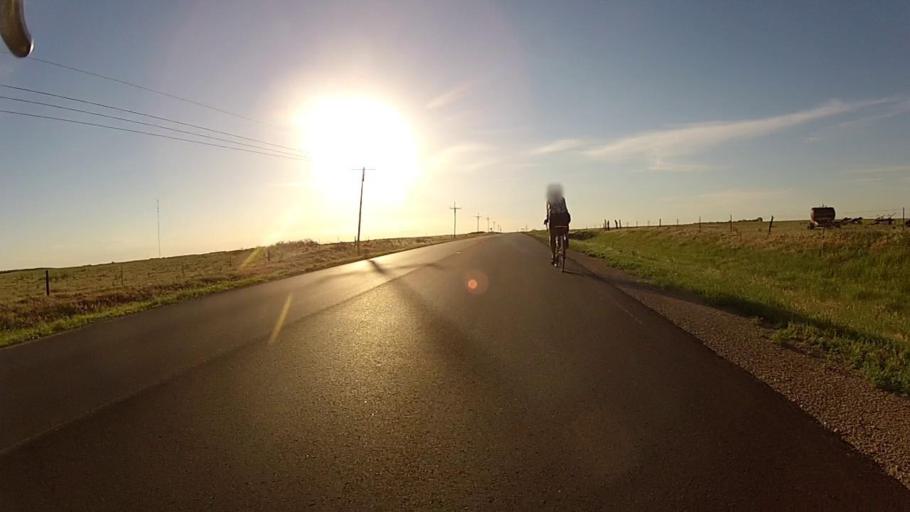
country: US
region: Kansas
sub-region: Comanche County
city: Coldwater
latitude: 37.2812
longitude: -99.2253
